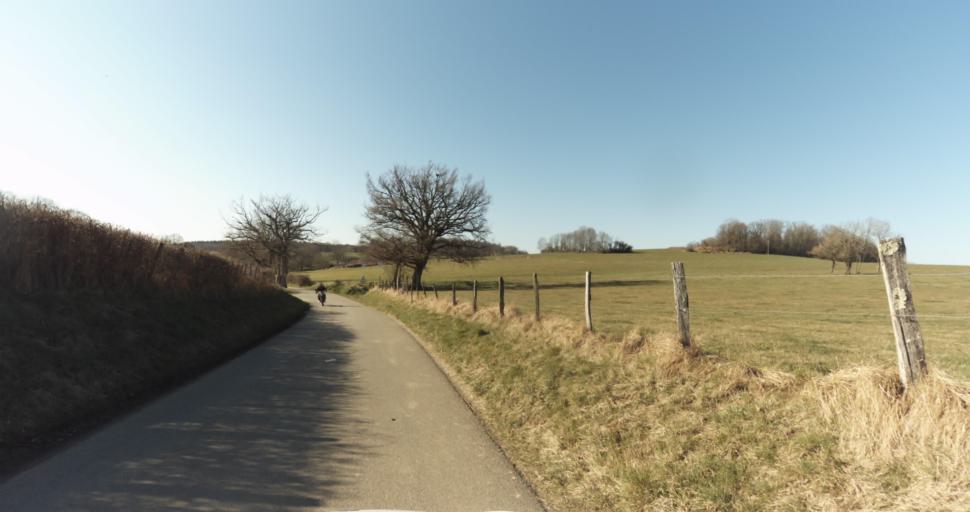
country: FR
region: Franche-Comte
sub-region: Departement du Jura
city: Montmorot
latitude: 46.6957
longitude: 5.5231
